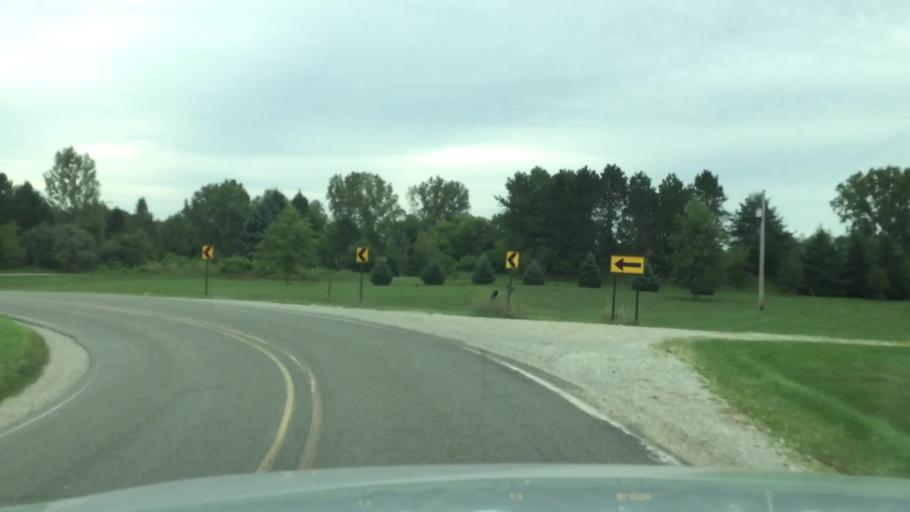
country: US
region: Michigan
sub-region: Shiawassee County
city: Durand
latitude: 42.8299
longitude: -84.0295
